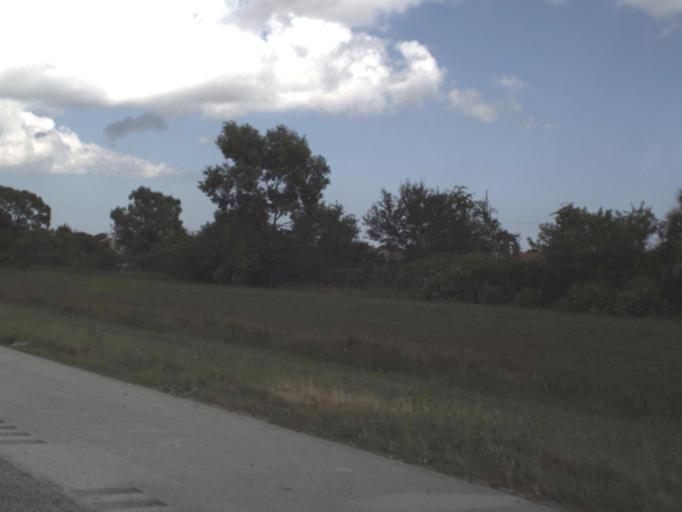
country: US
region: Florida
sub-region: Saint Lucie County
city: White City
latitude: 27.3545
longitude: -80.3746
